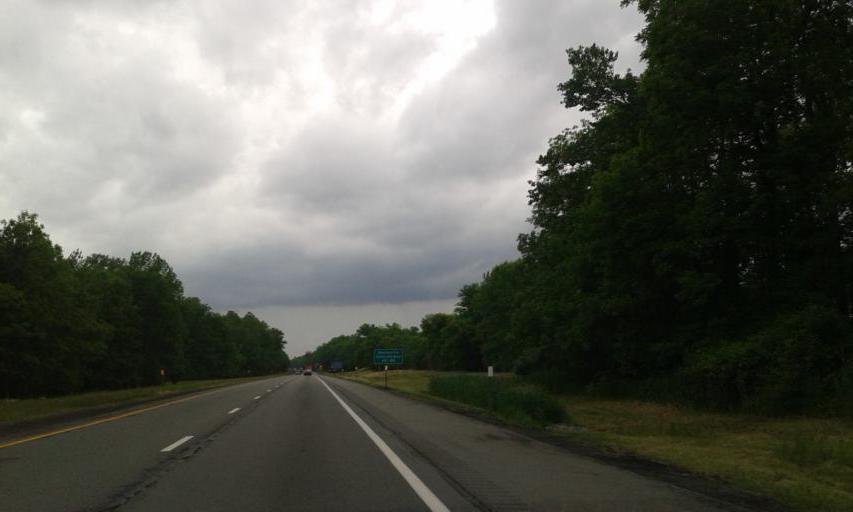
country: US
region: New York
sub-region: Ontario County
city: Shortsville
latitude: 42.9775
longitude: -77.2038
